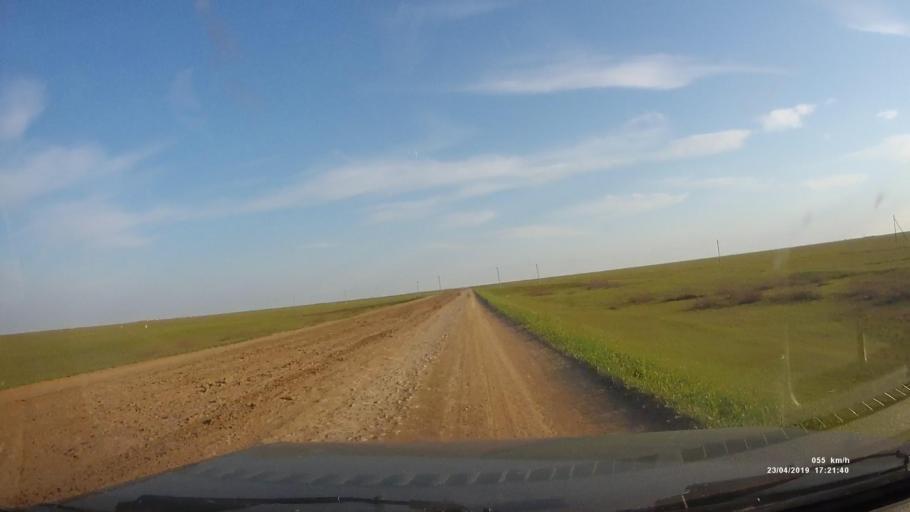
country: RU
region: Kalmykiya
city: Priyutnoye
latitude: 46.1743
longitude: 43.5056
